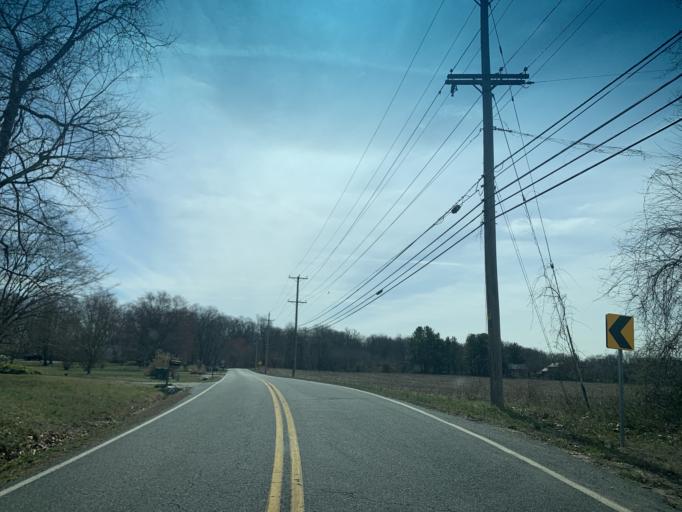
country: US
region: Maryland
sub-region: Cecil County
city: Charlestown
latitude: 39.5607
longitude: -76.0195
